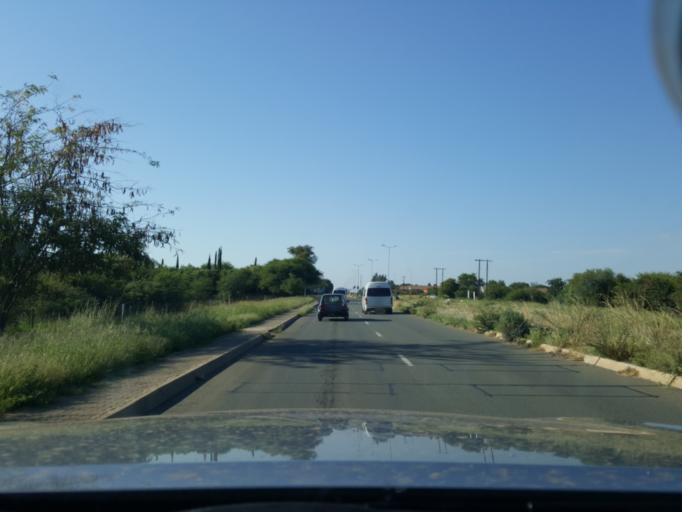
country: ZA
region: North-West
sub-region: Ngaka Modiri Molema District Municipality
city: Mmabatho
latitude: -25.8108
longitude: 25.6331
